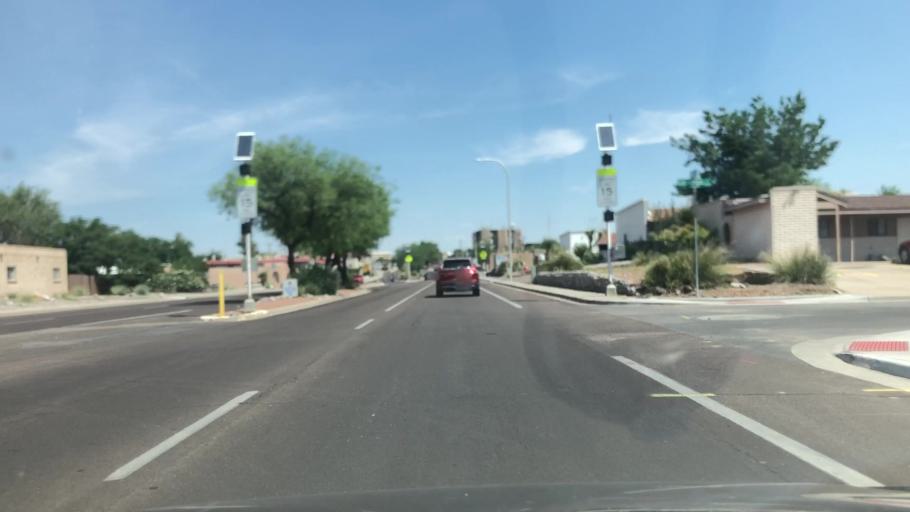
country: US
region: New Mexico
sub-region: Dona Ana County
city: University Park
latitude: 32.3019
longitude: -106.7372
